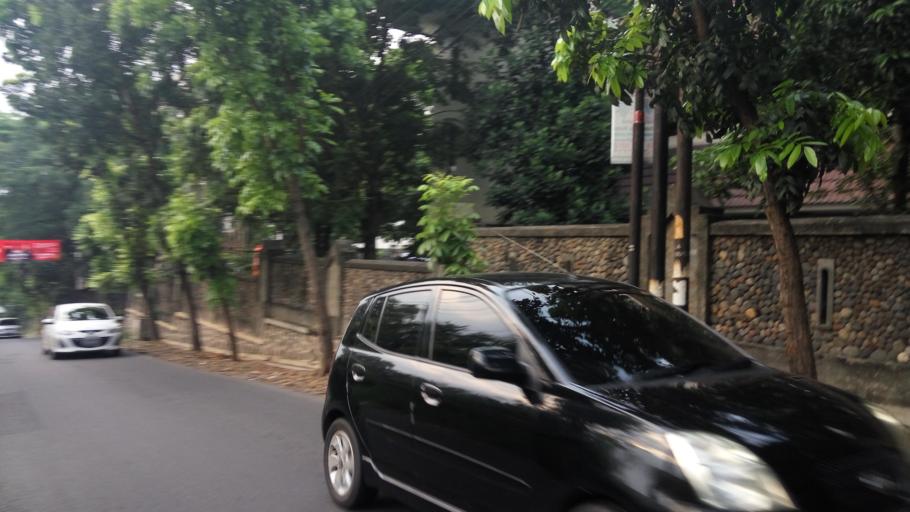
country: ID
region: Central Java
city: Semarang
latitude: -7.0261
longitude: 110.4050
